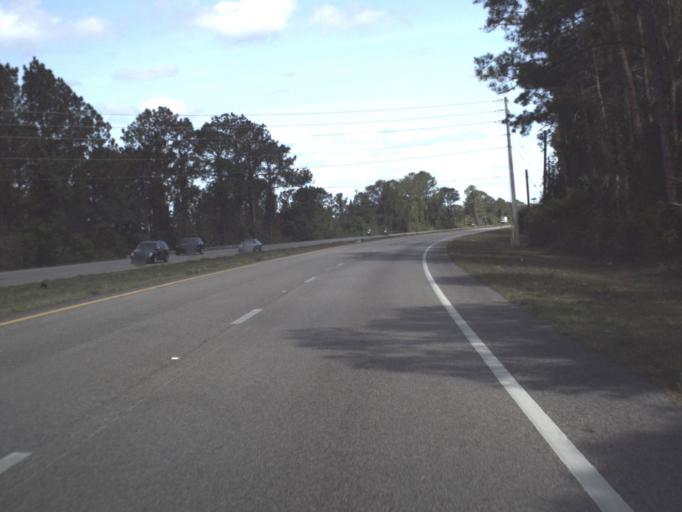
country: US
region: Florida
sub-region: Flagler County
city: Bunnell
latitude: 29.3842
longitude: -81.1878
